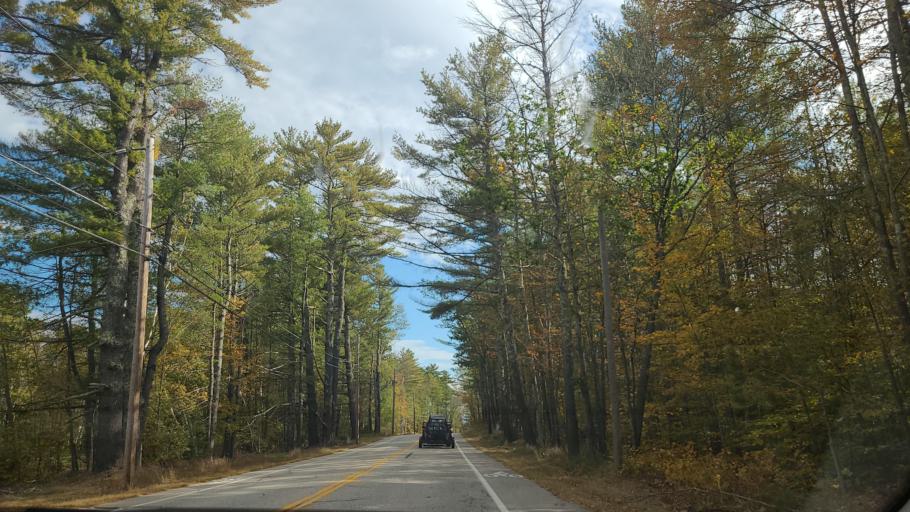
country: US
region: New Hampshire
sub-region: Carroll County
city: North Conway
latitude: 44.0232
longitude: -71.1313
